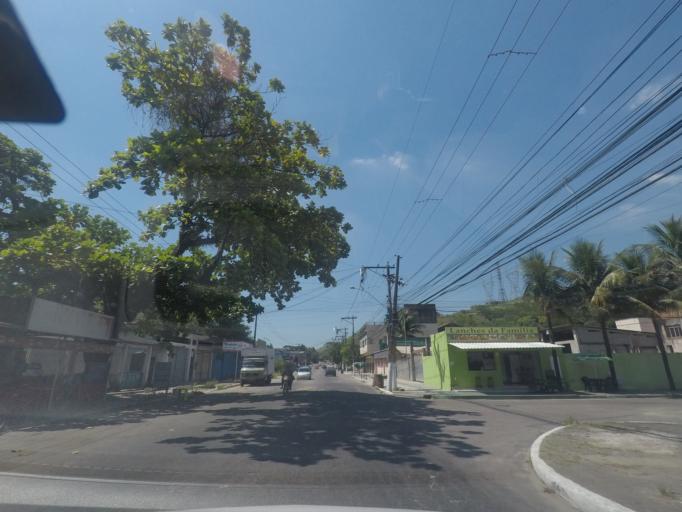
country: BR
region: Rio de Janeiro
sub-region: Petropolis
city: Petropolis
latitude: -22.5972
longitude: -43.1874
